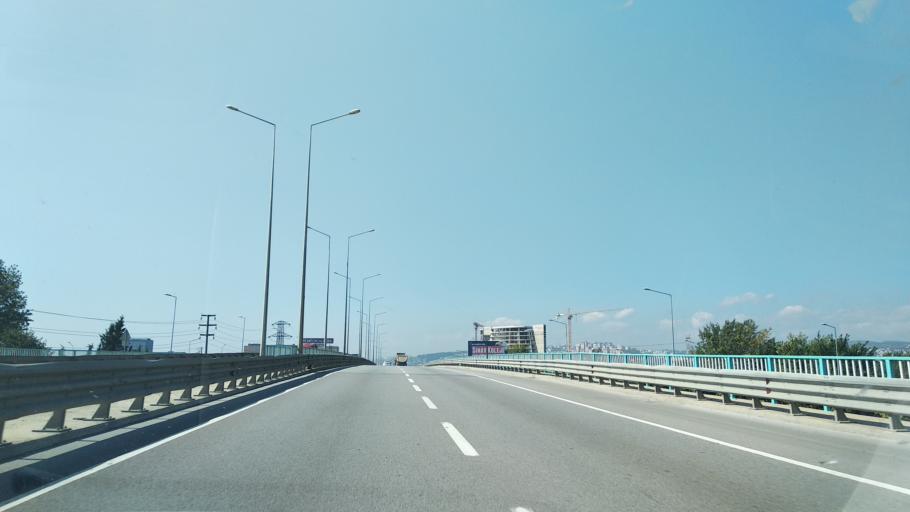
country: TR
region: Kocaeli
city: Kosekoy
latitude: 40.7584
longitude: 29.9902
